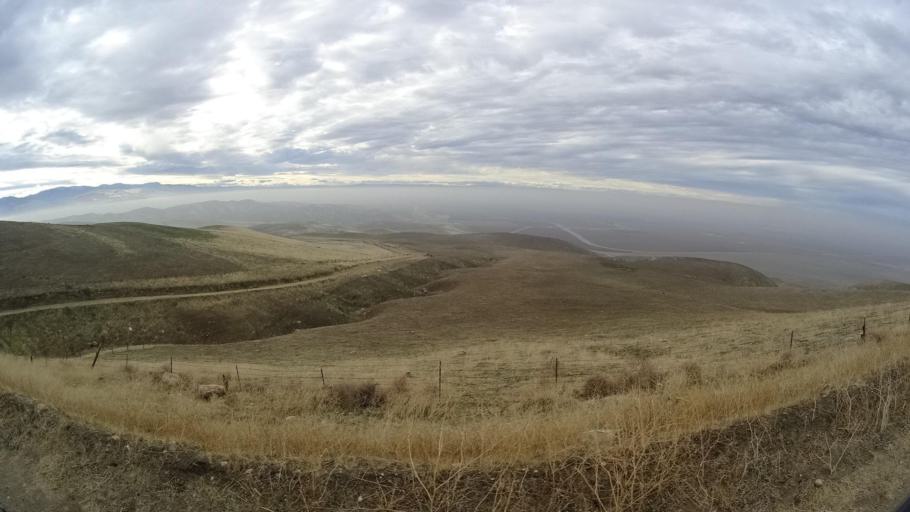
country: US
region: California
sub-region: Kern County
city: Arvin
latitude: 35.1382
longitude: -118.7866
